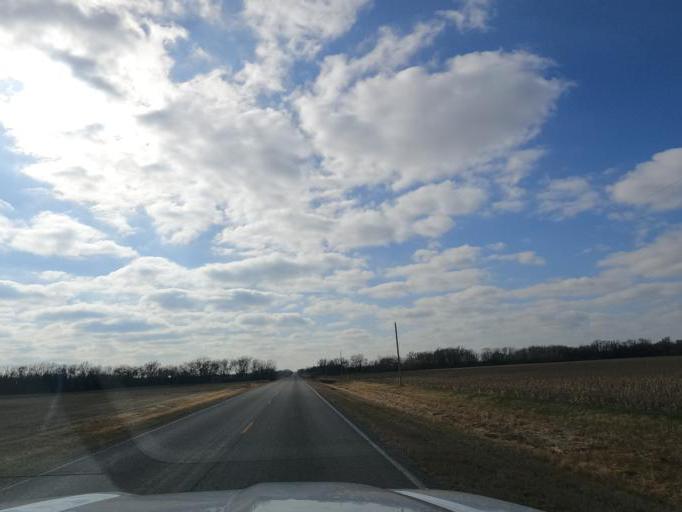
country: US
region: Kansas
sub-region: McPherson County
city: Inman
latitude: 38.2320
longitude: -97.8588
